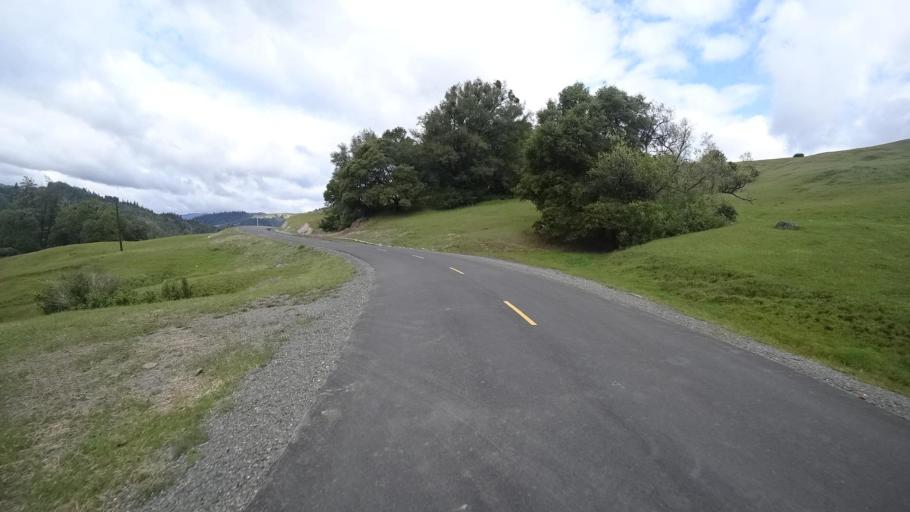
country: US
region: California
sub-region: Humboldt County
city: Redway
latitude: 40.2302
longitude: -123.6143
